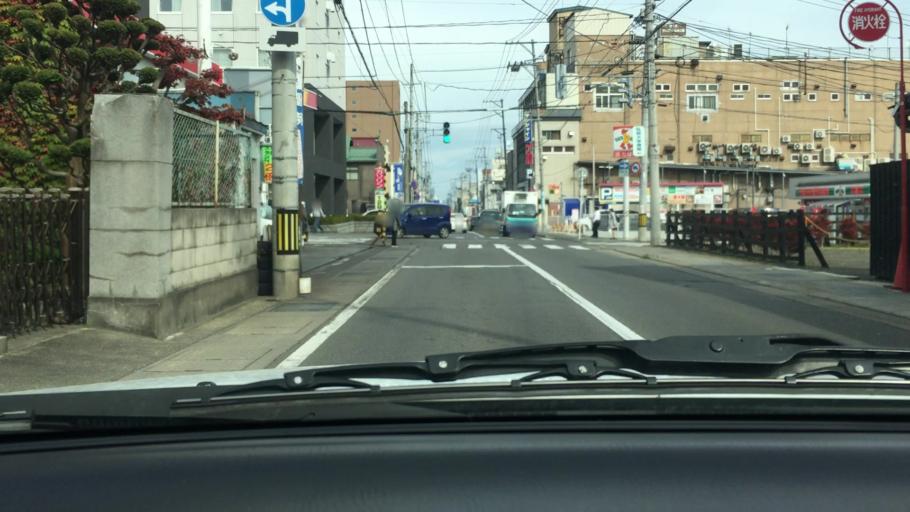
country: JP
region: Aomori
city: Hirosaki
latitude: 40.6001
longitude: 140.4687
